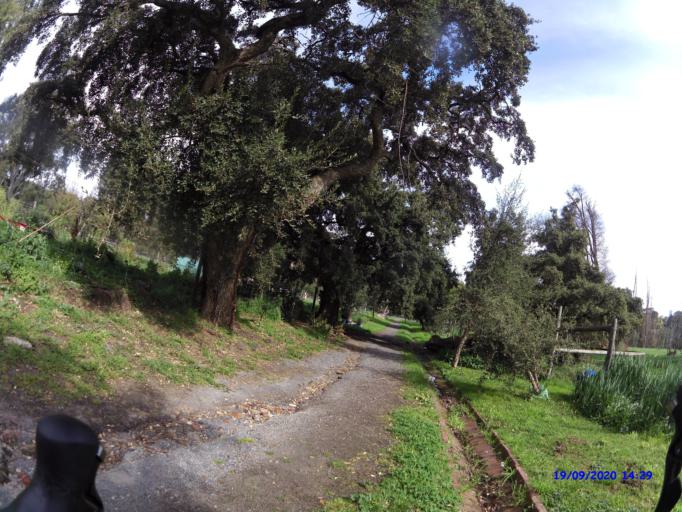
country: AU
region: Victoria
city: Abbotsford
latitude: -37.8035
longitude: 145.0030
